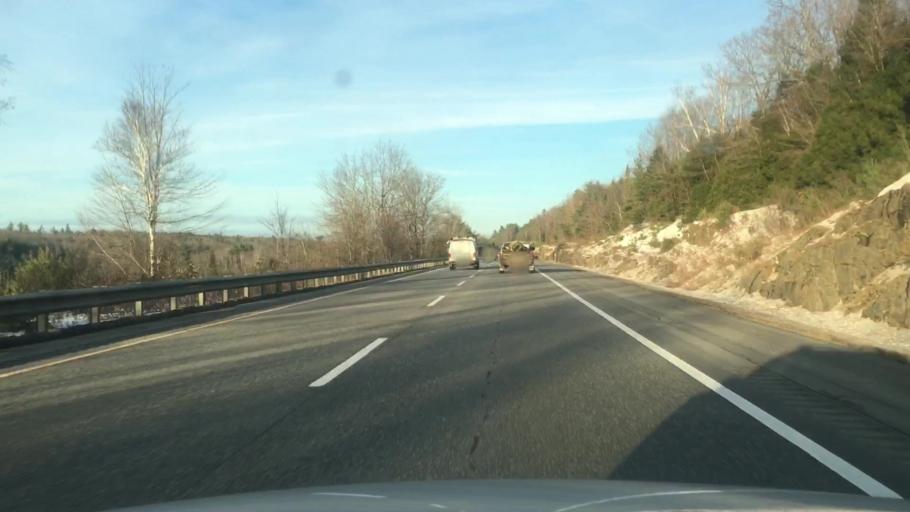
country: US
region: Maine
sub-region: Kennebec County
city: Sidney
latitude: 44.3797
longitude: -69.7679
